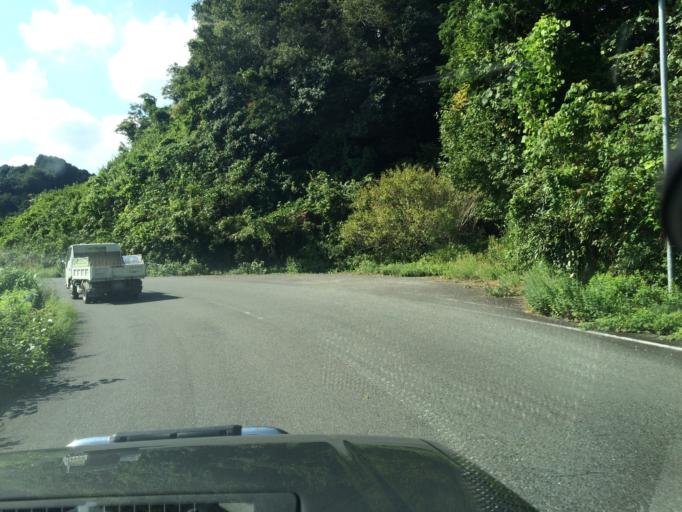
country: JP
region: Mie
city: Nabari
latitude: 34.6989
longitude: 135.9740
